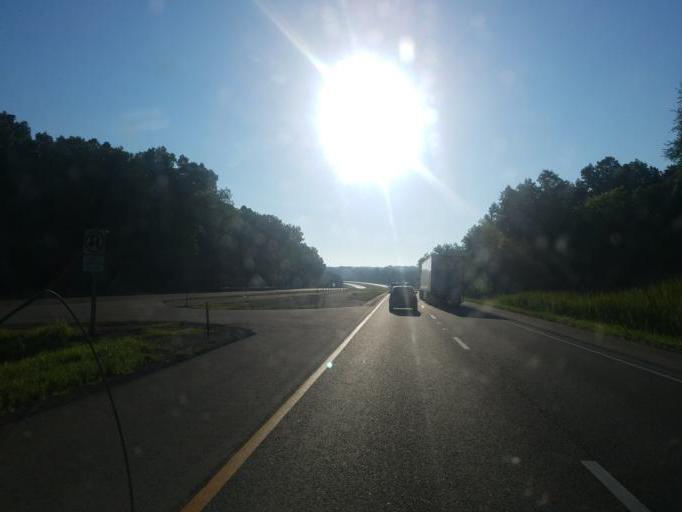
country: US
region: Illinois
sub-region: Bond County
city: Greenville
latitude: 38.9159
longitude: -89.2595
